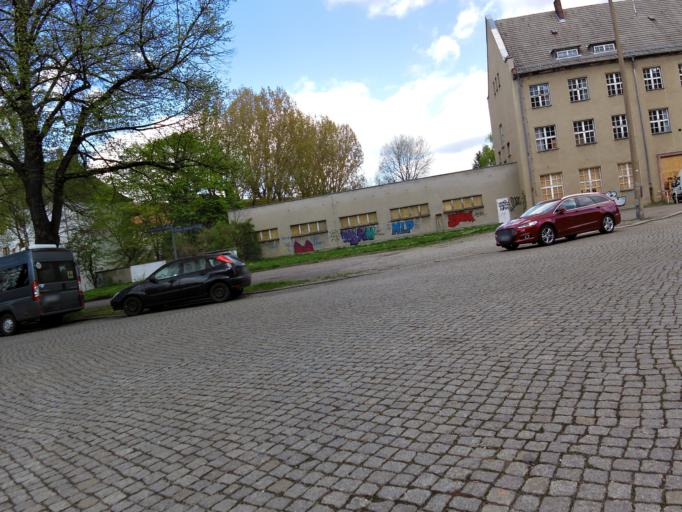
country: DE
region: Saxony
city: Leipzig
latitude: 51.3361
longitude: 12.4183
